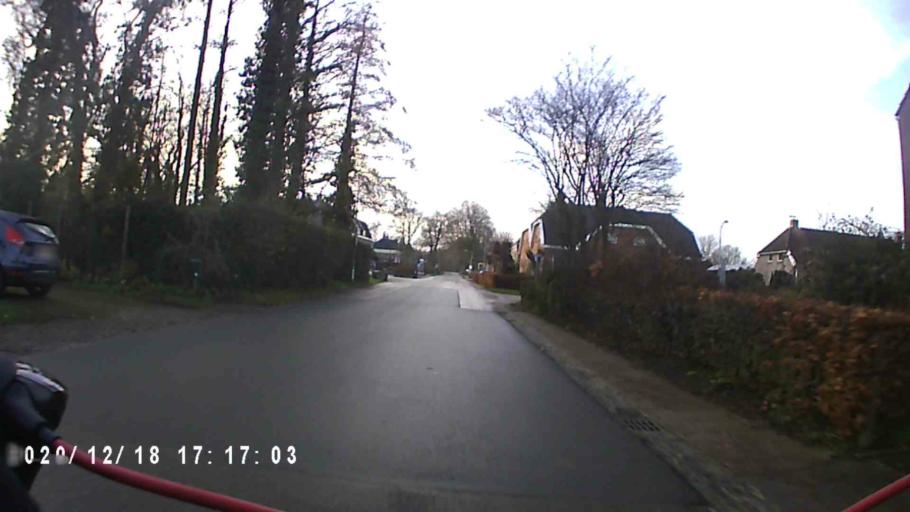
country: NL
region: Drenthe
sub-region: Gemeente Tynaarlo
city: Tynaarlo
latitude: 53.0788
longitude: 6.6126
